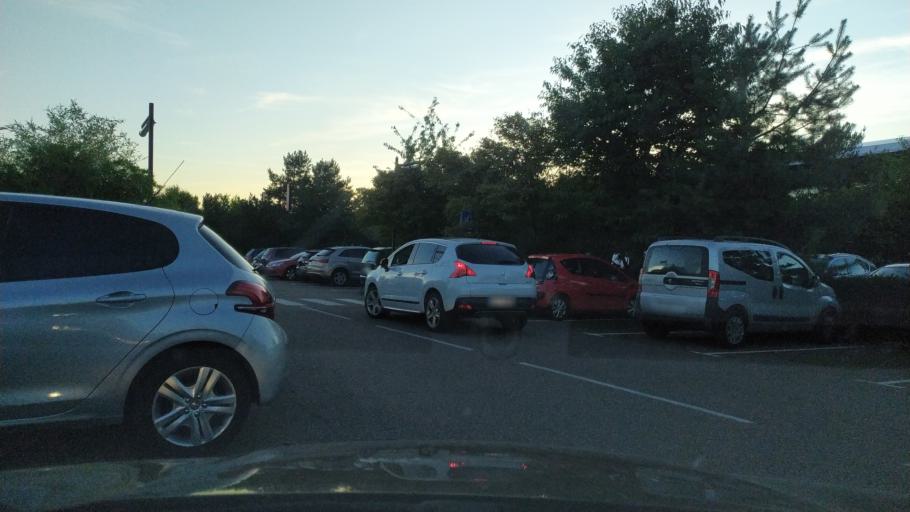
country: FR
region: Lorraine
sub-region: Departement de la Moselle
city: Moulins-les-Metz
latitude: 49.0821
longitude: 6.1029
